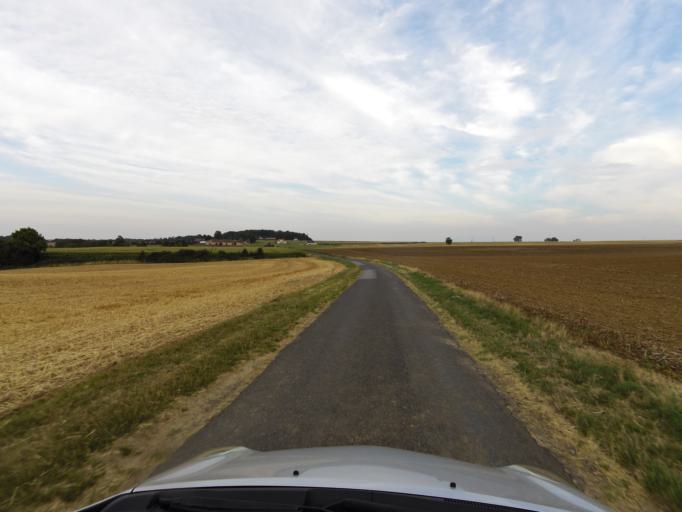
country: FR
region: Picardie
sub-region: Departement de l'Aisne
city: Bruyeres-et-Montberault
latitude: 49.4998
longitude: 3.6578
